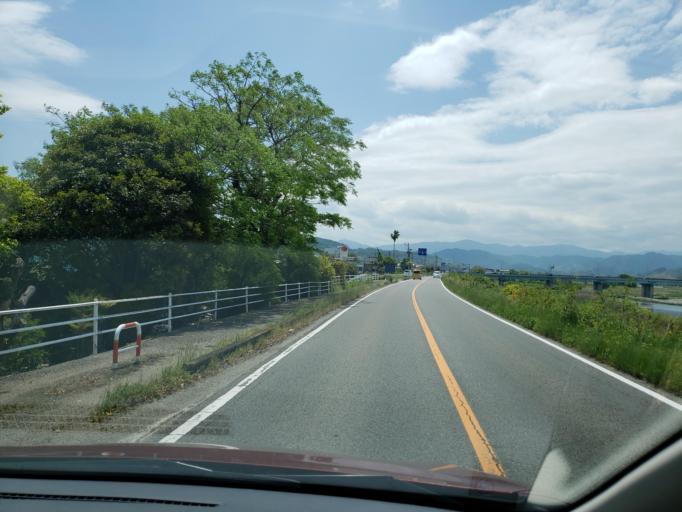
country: JP
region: Tokushima
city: Tokushima-shi
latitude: 34.0755
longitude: 134.5014
